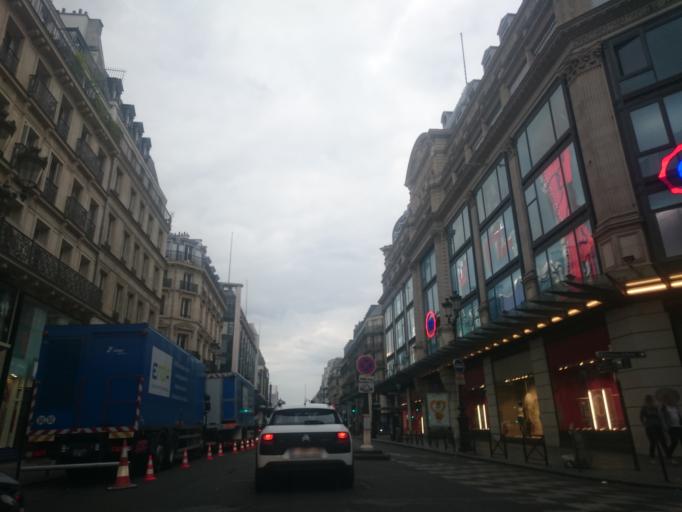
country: FR
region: Ile-de-France
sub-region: Paris
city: Paris
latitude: 48.8593
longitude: 2.3457
